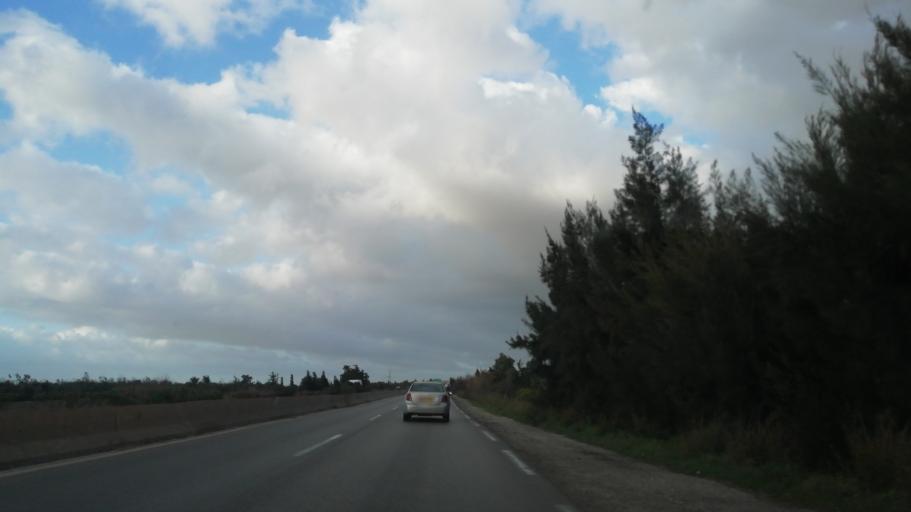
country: DZ
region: Oran
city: Bou Tlelis
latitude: 35.5671
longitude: -0.8935
